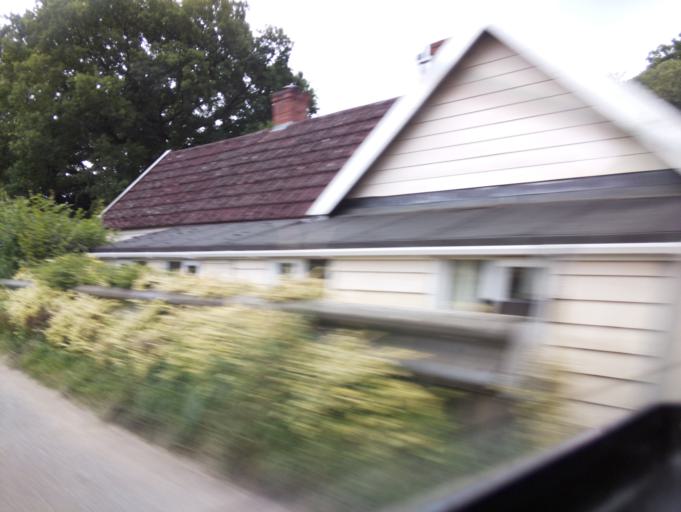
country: GB
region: England
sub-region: Gloucestershire
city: Shurdington
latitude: 51.7905
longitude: -2.1164
